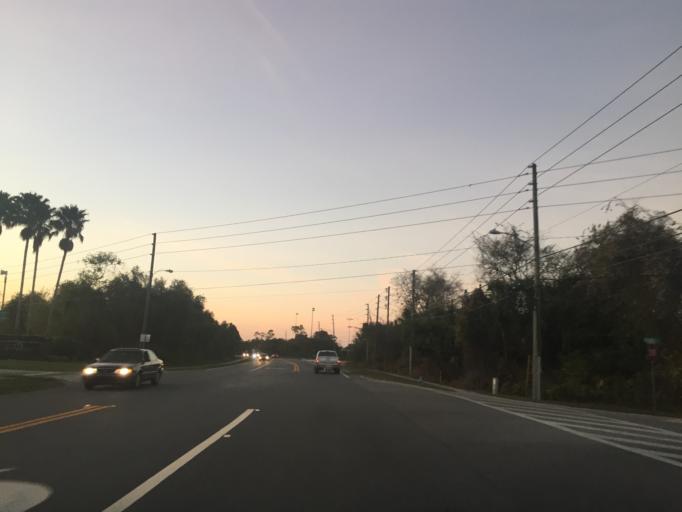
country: US
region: Florida
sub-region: Seminole County
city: Oviedo
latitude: 28.6664
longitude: -81.1846
